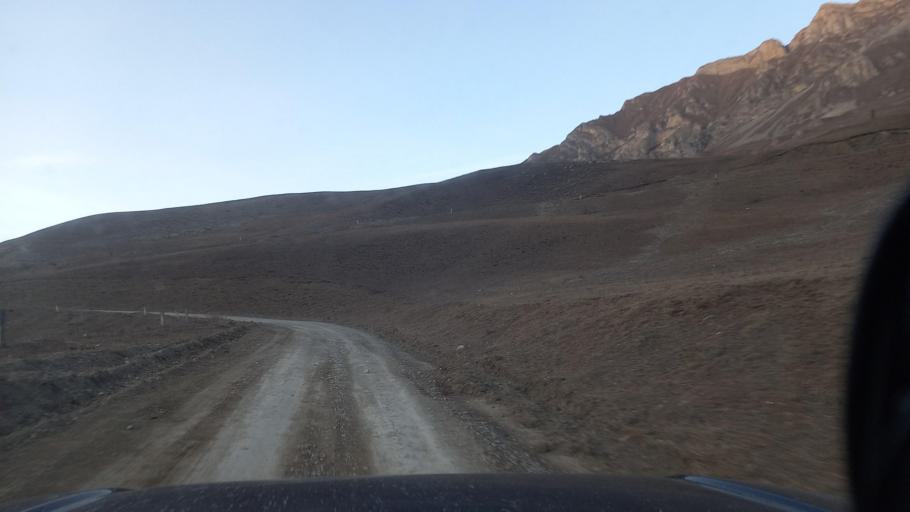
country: RU
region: Ingushetiya
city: Dzhayrakh
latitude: 42.8385
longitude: 44.5424
